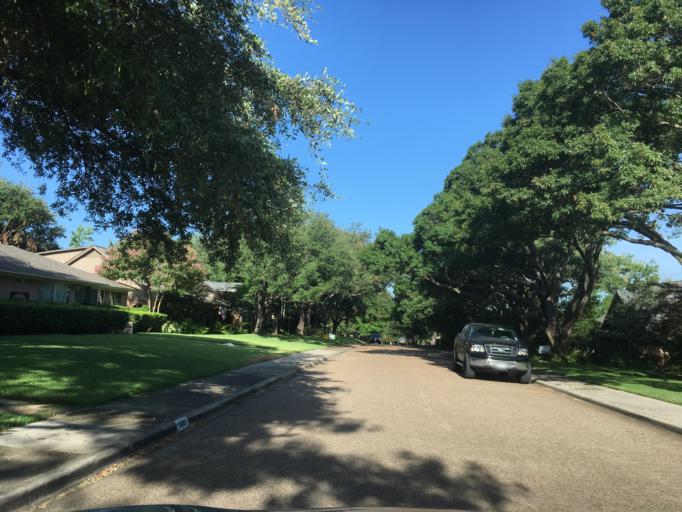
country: US
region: Texas
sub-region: Dallas County
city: Richardson
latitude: 32.8838
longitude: -96.7259
